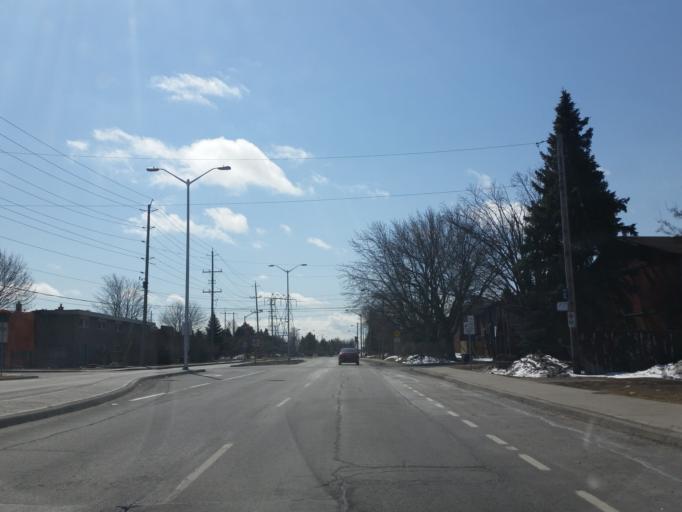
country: CA
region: Ontario
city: Bells Corners
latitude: 45.3211
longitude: -75.8328
